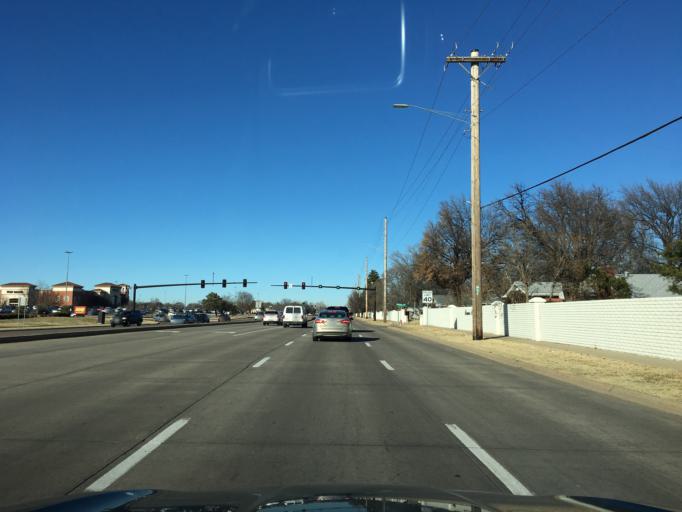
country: US
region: Kansas
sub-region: Sedgwick County
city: Bellaire
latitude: 37.6807
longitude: -97.2444
